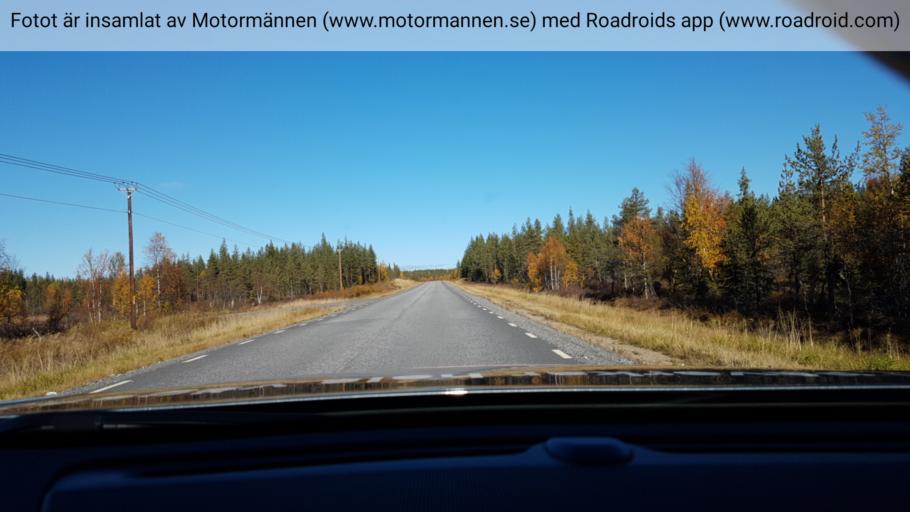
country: SE
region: Norrbotten
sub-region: Gallivare Kommun
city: Gaellivare
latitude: 66.7954
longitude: 21.0388
